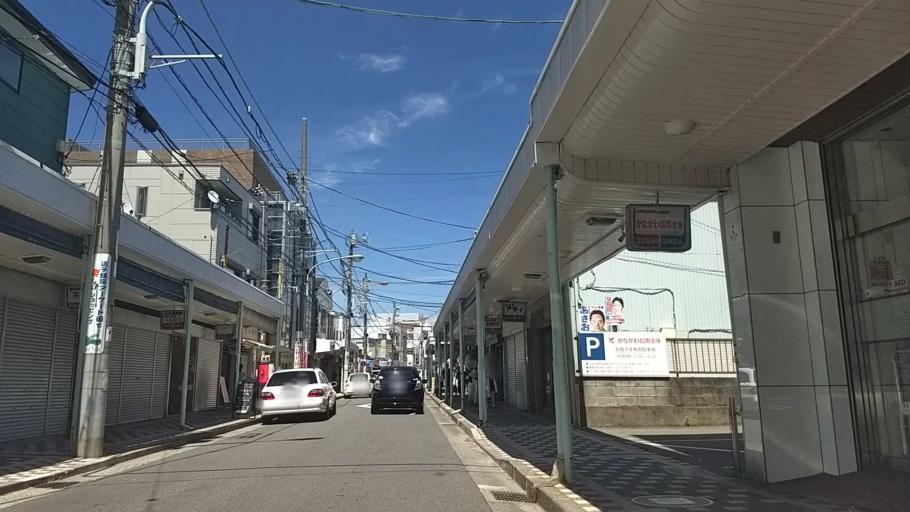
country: JP
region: Kanagawa
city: Zushi
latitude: 35.2950
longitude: 139.5778
